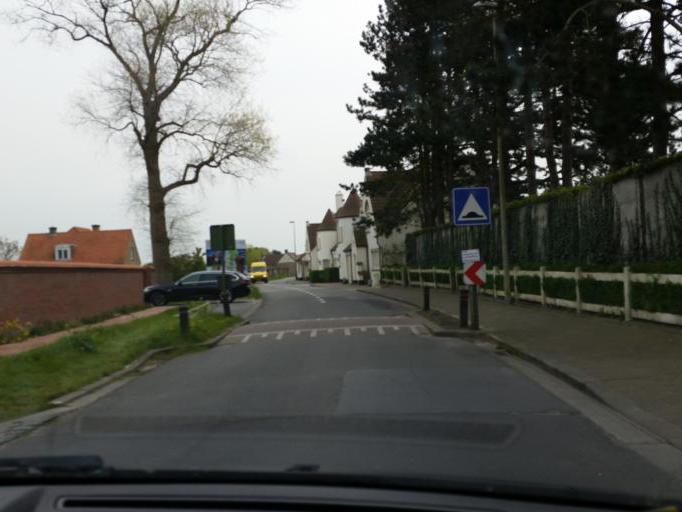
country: BE
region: Flanders
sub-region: Provincie West-Vlaanderen
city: Knokke-Heist
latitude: 51.3388
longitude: 3.3170
